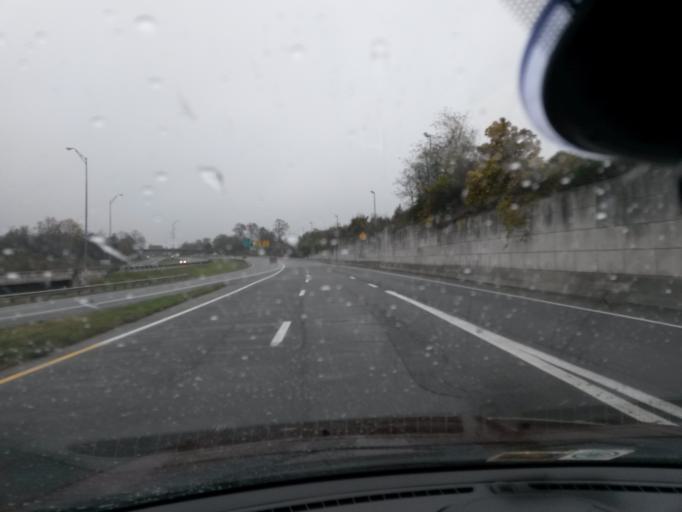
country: US
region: Virginia
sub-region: Montgomery County
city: Christiansburg
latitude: 37.1528
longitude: -80.4104
